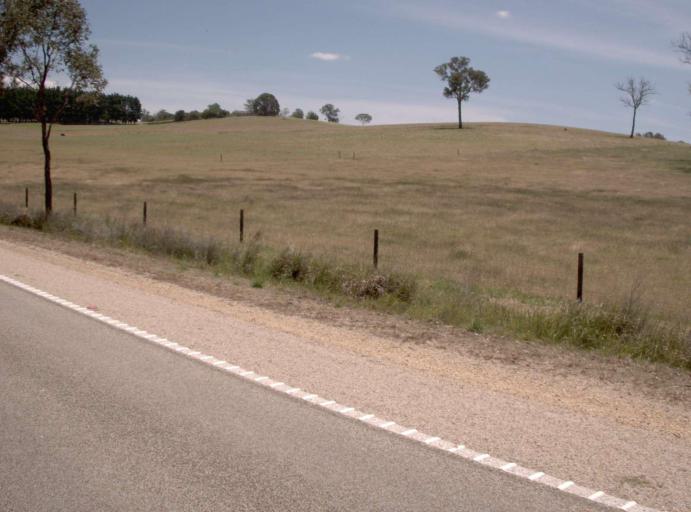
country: AU
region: Victoria
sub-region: East Gippsland
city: Bairnsdale
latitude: -37.7652
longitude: 147.6980
